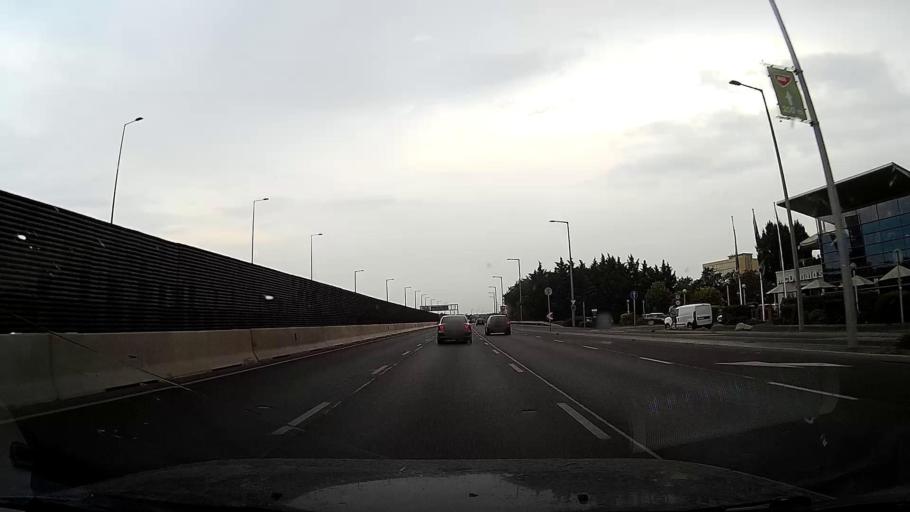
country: HU
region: Budapest
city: Budapest XI. keruelet
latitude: 47.4658
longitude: 19.0134
